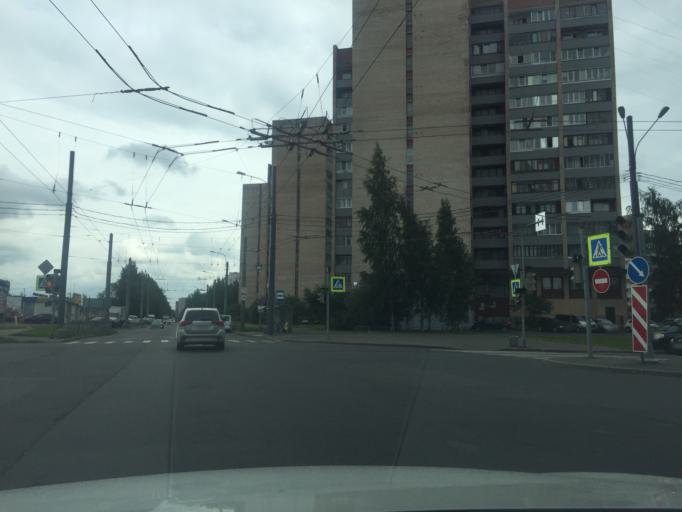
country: RU
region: Leningrad
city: Parnas
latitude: 60.0558
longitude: 30.3594
